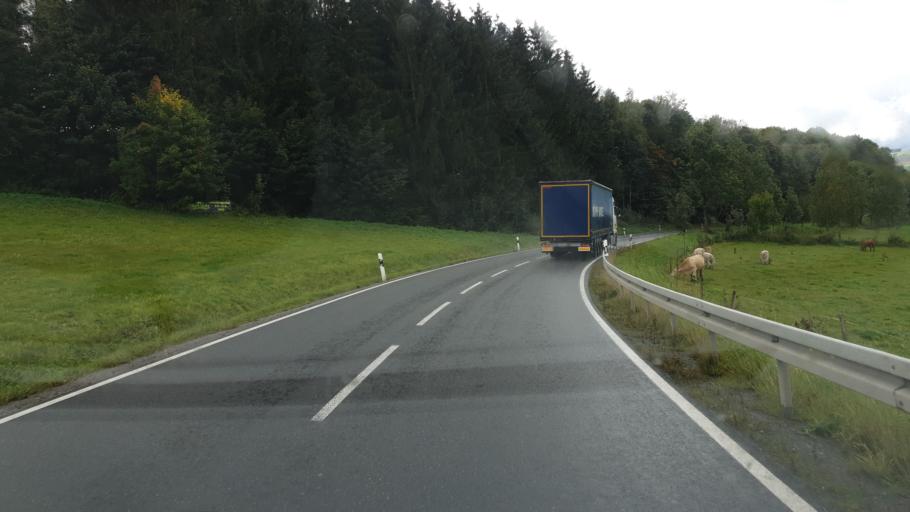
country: DE
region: Saxony
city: Pockau
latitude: 50.7094
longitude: 13.2412
